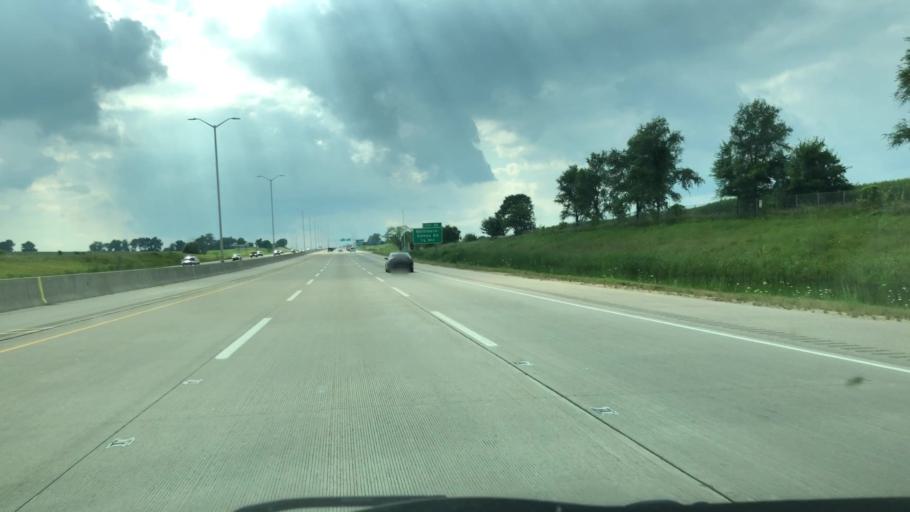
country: US
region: Illinois
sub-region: Boone County
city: Belvidere
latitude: 42.2344
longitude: -88.7992
